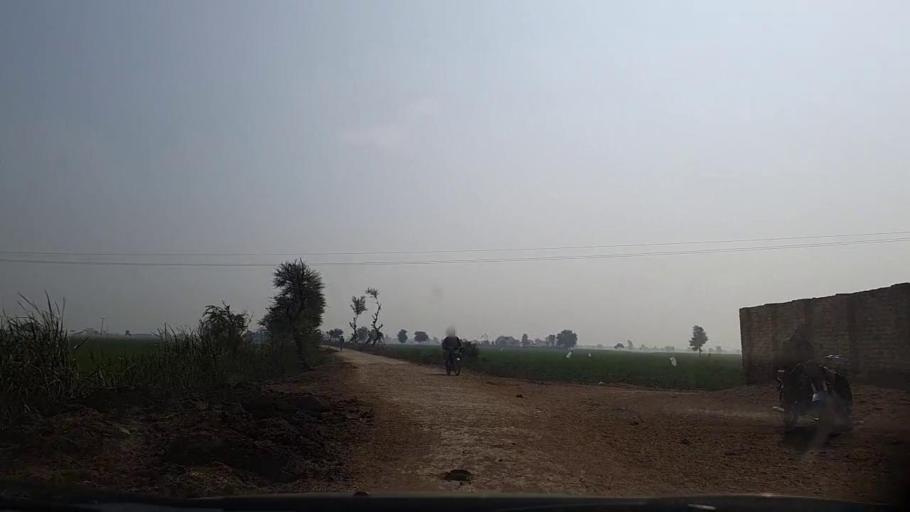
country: PK
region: Sindh
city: Sanghar
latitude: 26.0521
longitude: 68.9742
